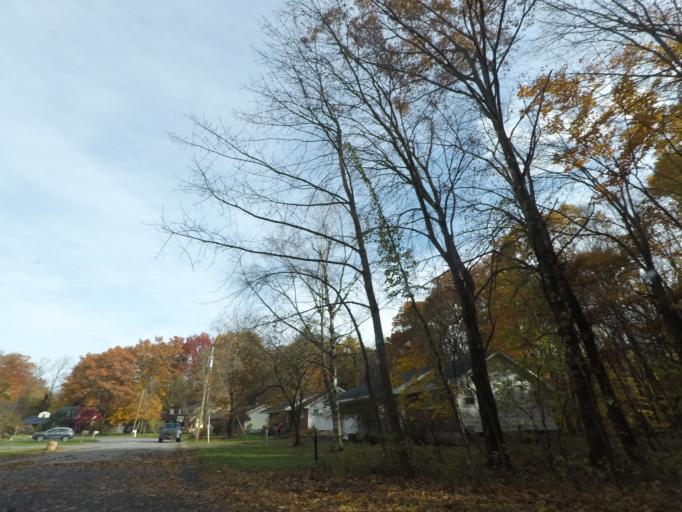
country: US
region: New York
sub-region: Schenectady County
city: Rotterdam
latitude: 42.7659
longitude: -73.9702
